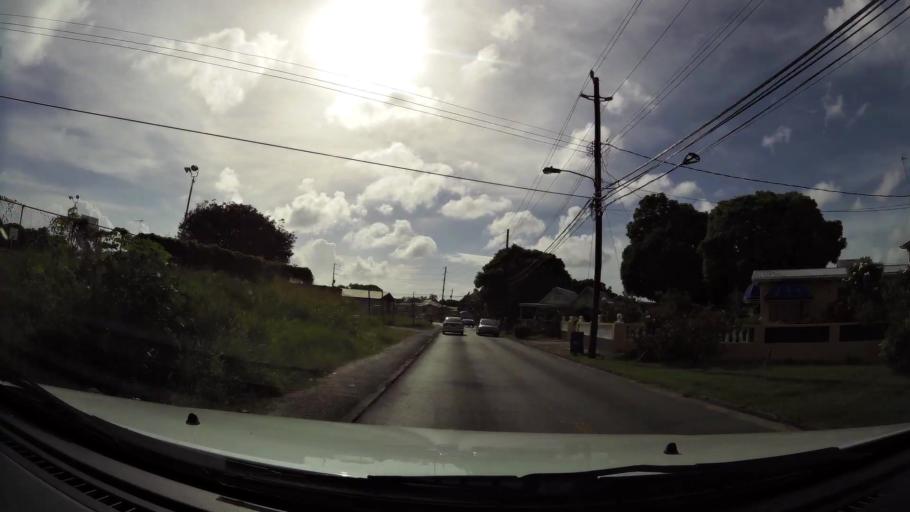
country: BB
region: Saint Michael
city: Bridgetown
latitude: 13.0846
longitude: -59.5918
